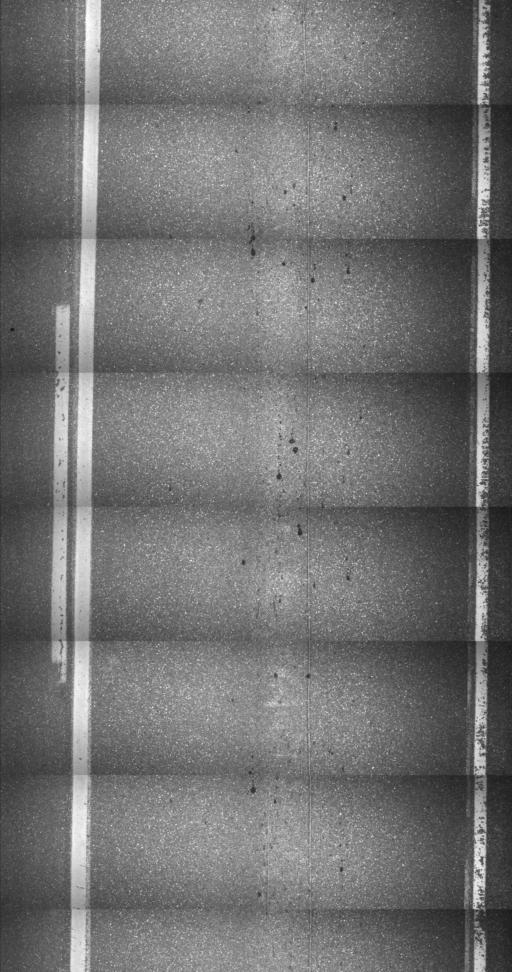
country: US
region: Vermont
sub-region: Essex County
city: Guildhall
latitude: 44.5527
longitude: -71.5965
